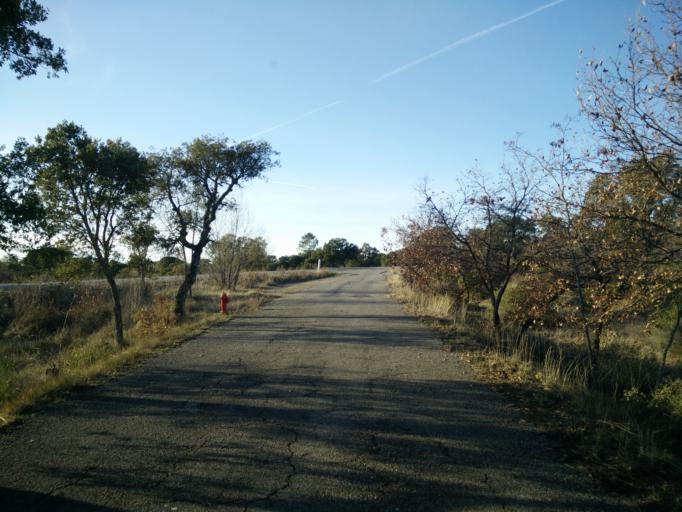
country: FR
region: Provence-Alpes-Cote d'Azur
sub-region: Departement du Var
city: La Garde-Freinet
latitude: 43.3552
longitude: 6.4111
